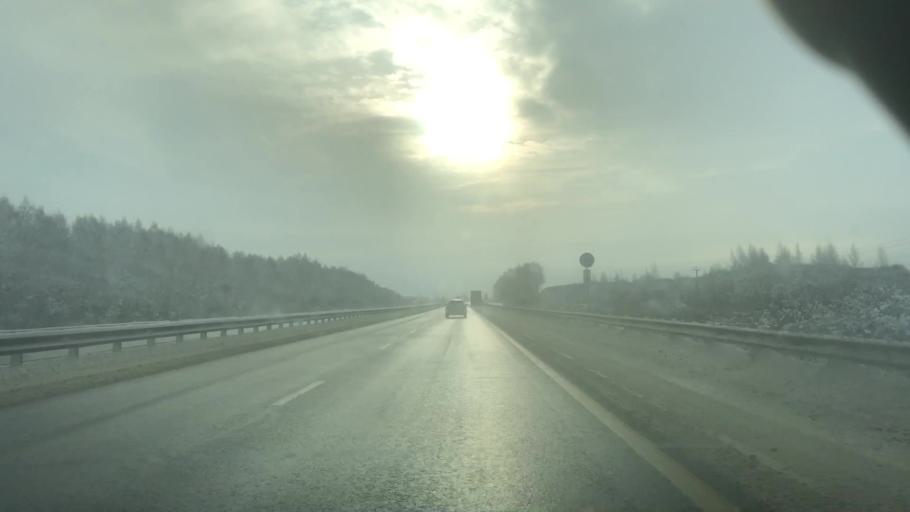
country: RU
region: Tula
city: Venev
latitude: 54.2880
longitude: 38.1585
